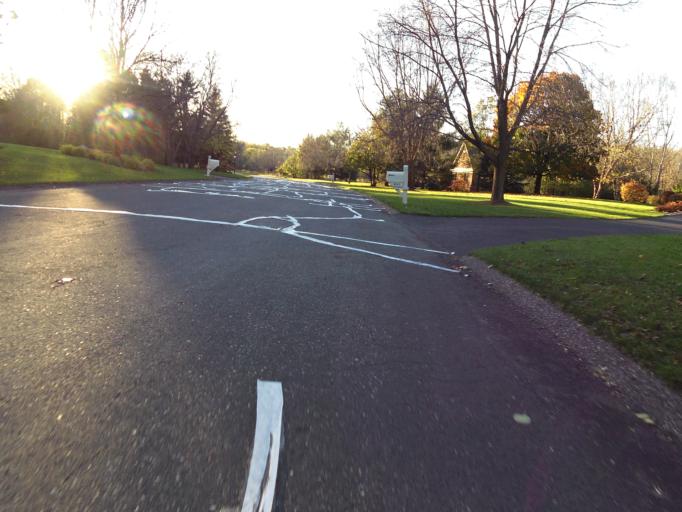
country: US
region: Minnesota
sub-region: Washington County
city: Lakeland
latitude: 44.9613
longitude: -92.8202
